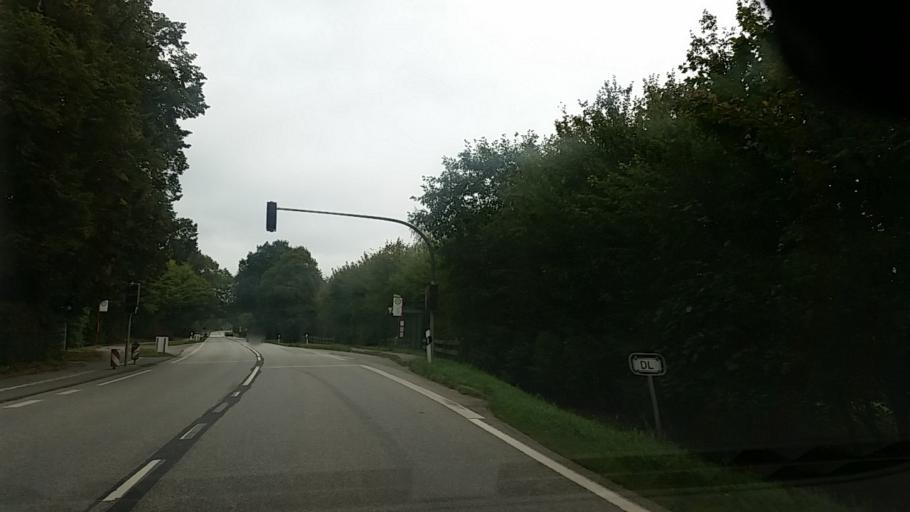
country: DE
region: Schleswig-Holstein
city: Hasenmoor
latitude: 53.9011
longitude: 9.9978
